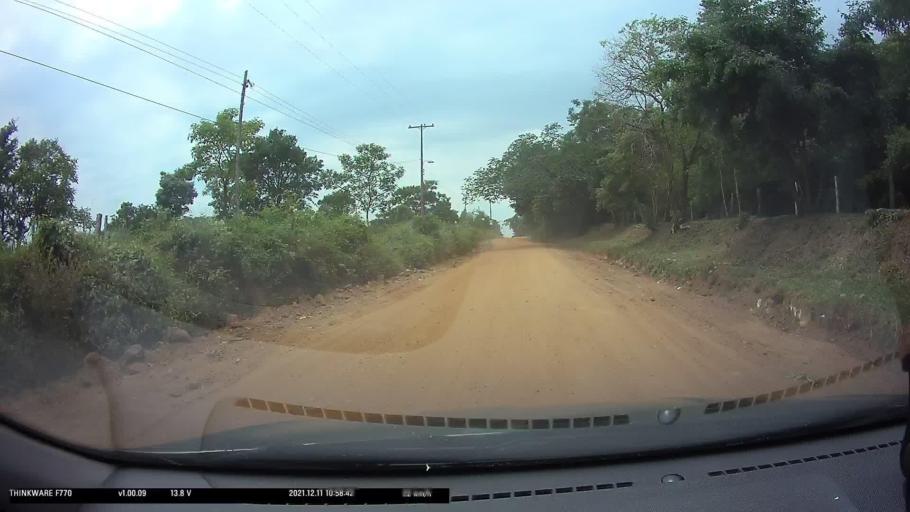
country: PY
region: Cordillera
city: San Bernardino
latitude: -25.3045
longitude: -57.2554
